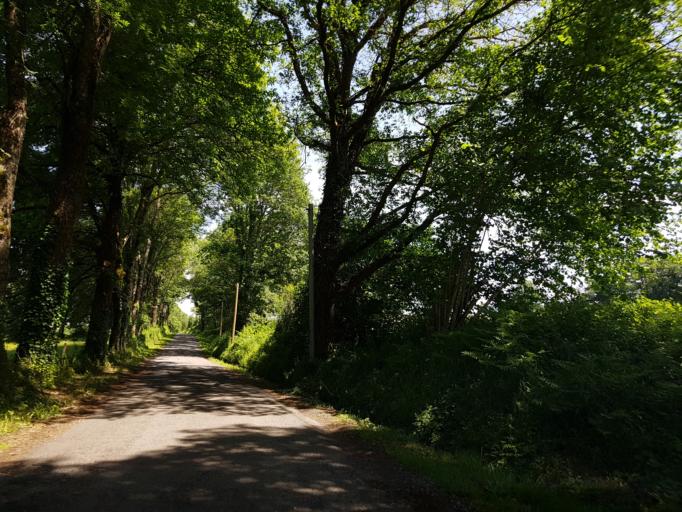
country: FR
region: Poitou-Charentes
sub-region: Departement de la Charente
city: Chabanais
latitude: 45.8884
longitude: 0.7412
